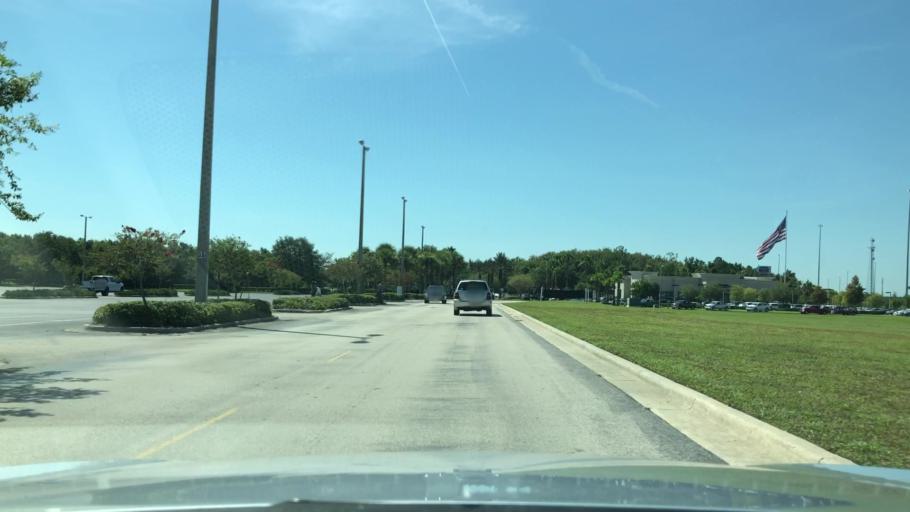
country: US
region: Florida
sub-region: Saint Johns County
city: Saint Augustine
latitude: 29.9251
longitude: -81.4139
